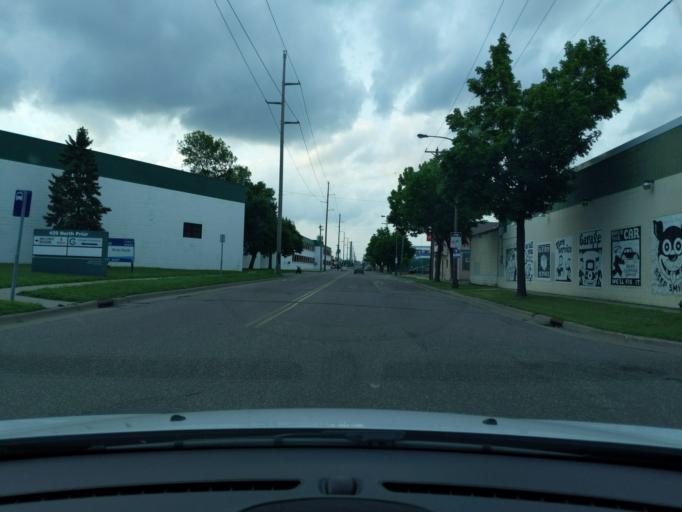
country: US
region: Minnesota
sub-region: Ramsey County
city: Falcon Heights
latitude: 44.9541
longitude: -93.1822
